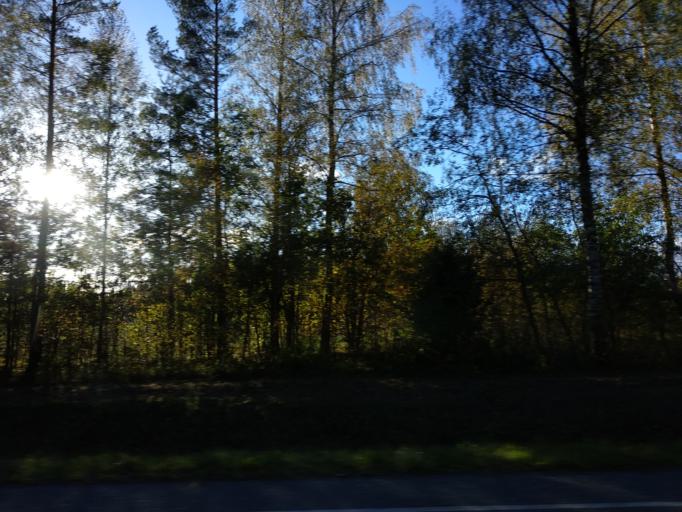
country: EE
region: Polvamaa
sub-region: Polva linn
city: Polva
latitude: 58.0344
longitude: 27.0661
